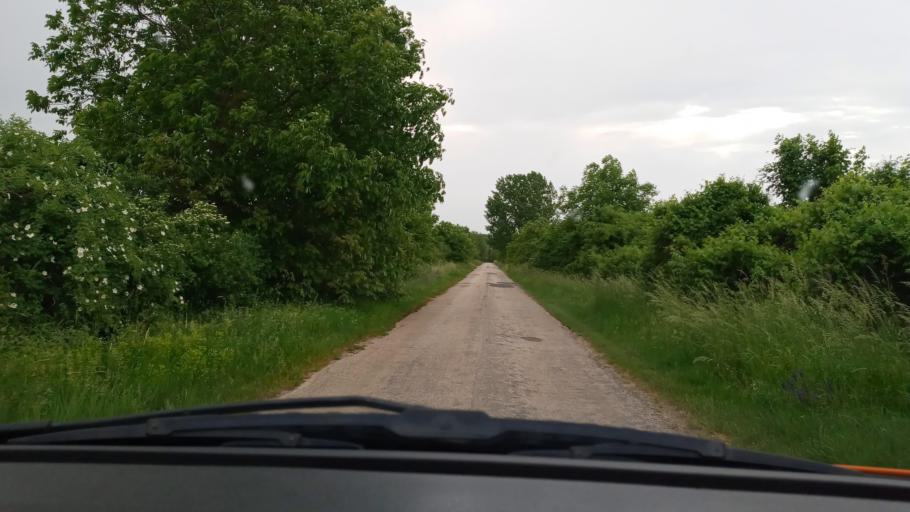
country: HU
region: Baranya
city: Harkany
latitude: 45.9046
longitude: 18.1380
